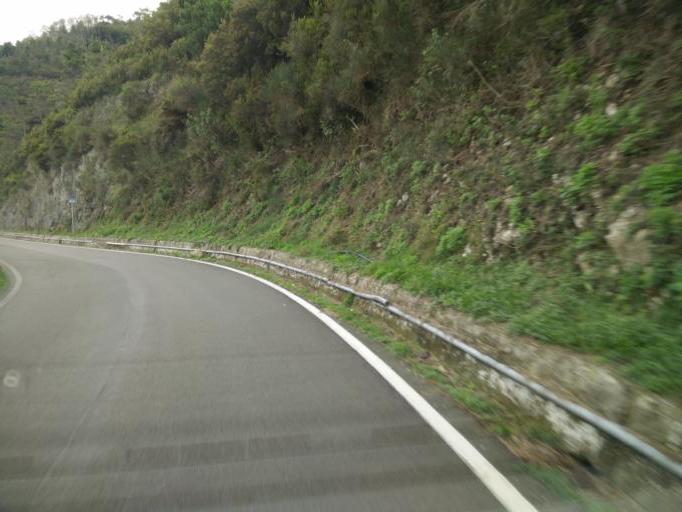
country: IT
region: Liguria
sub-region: Provincia di La Spezia
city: Riomaggiore
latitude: 44.1180
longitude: 9.7262
